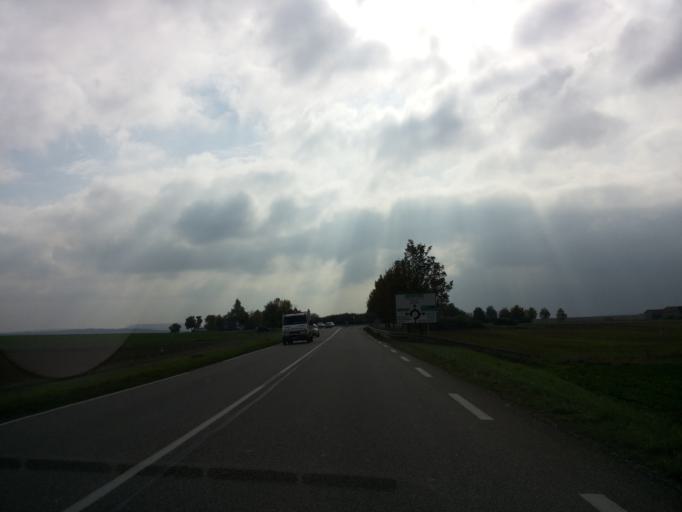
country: FR
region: Lorraine
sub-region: Departement de la Moselle
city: Solgne
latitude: 48.9855
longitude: 6.2867
